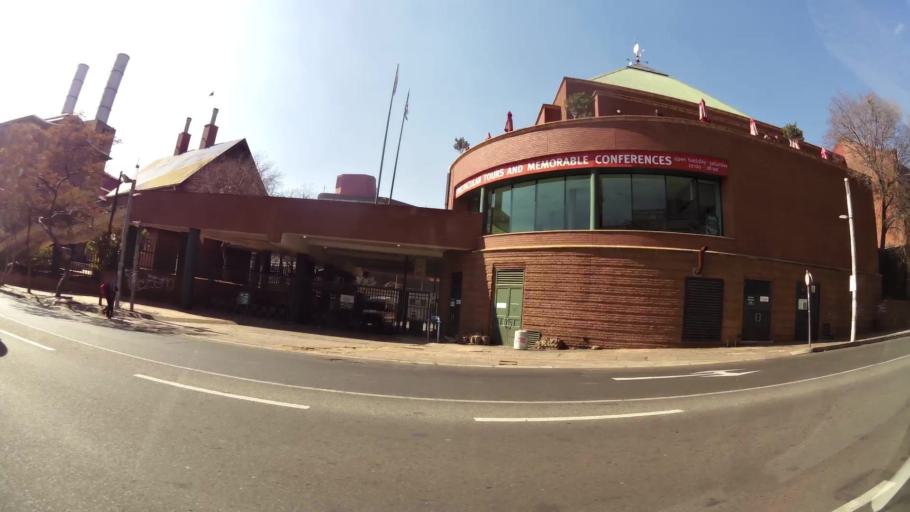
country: ZA
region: Gauteng
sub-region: City of Johannesburg Metropolitan Municipality
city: Johannesburg
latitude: -26.2043
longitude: 28.0334
